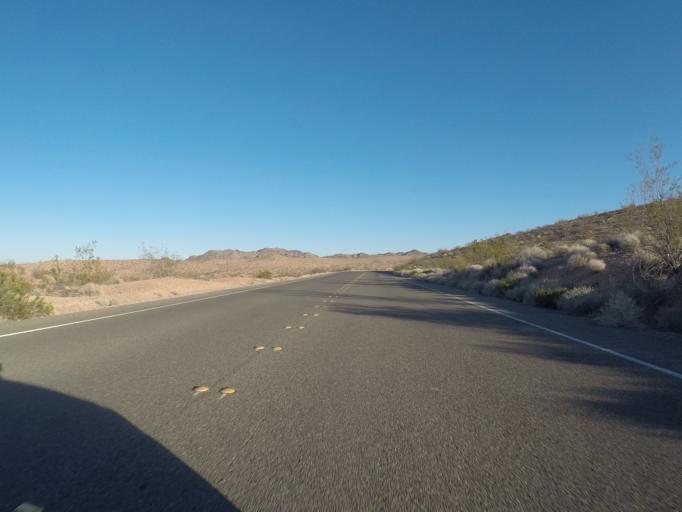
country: US
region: Nevada
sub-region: Clark County
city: Moapa Valley
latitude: 36.2752
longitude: -114.4855
